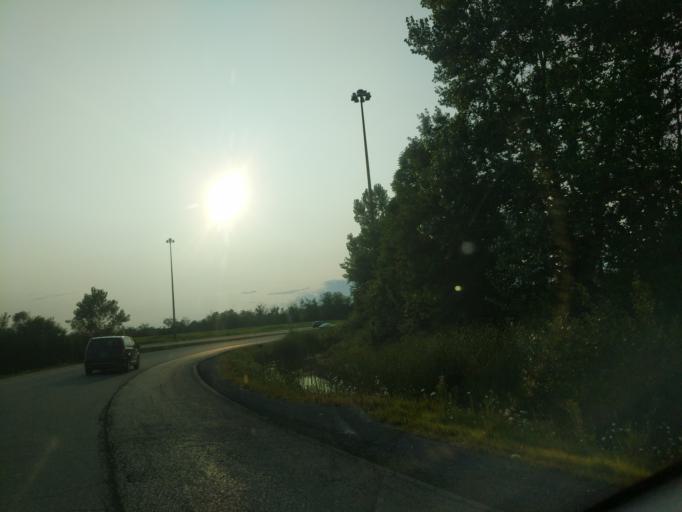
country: CA
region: Ontario
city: Bells Corners
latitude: 45.3153
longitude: -75.8021
